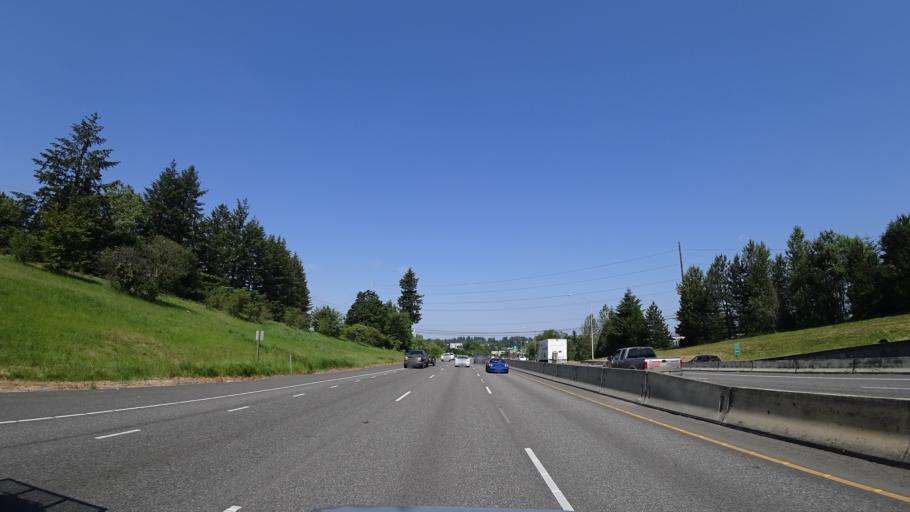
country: US
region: Oregon
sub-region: Washington County
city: Tigard
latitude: 45.4266
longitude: -122.7523
